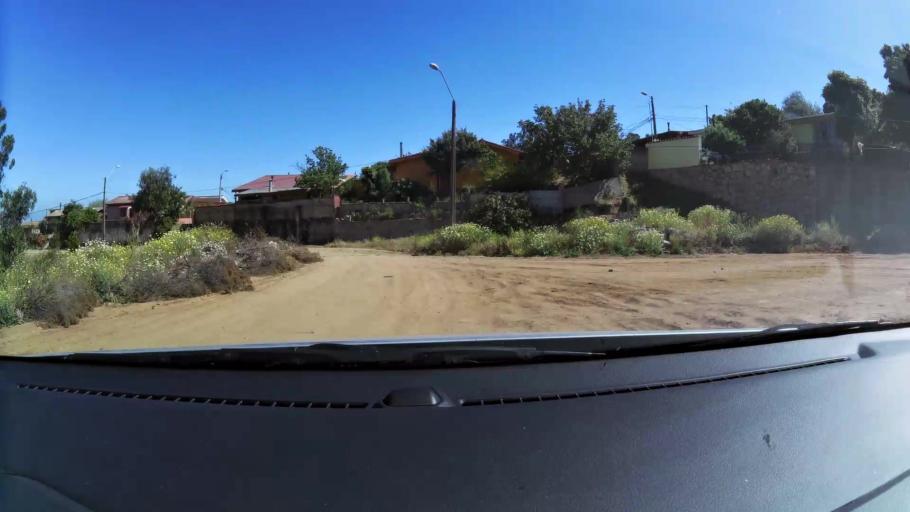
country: CL
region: Valparaiso
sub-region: Provincia de Valparaiso
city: Vina del Mar
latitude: -33.0641
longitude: -71.5781
